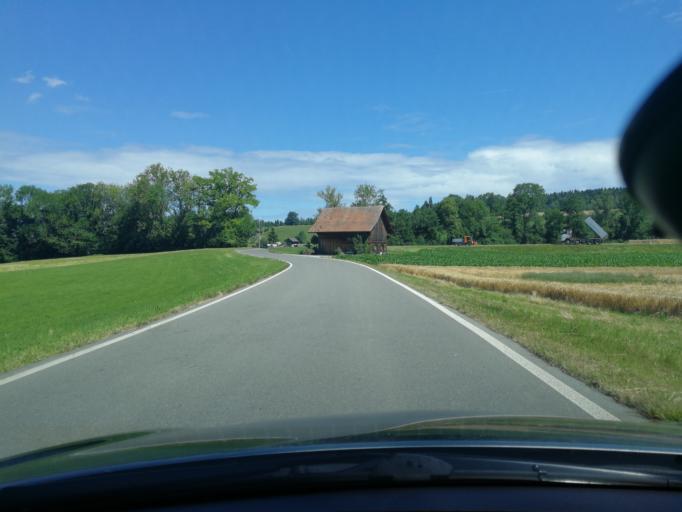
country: CH
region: Zurich
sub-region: Bezirk Meilen
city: Herrliberg
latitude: 47.2971
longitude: 8.6191
